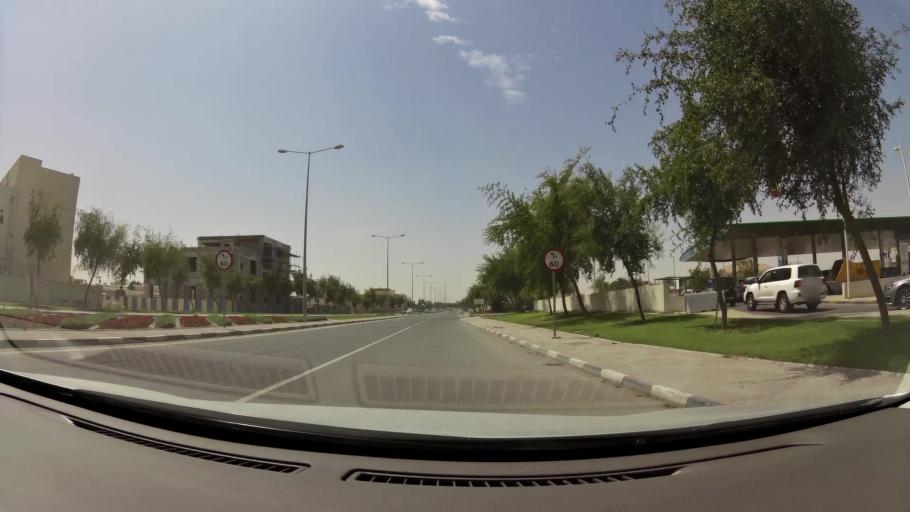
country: QA
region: Baladiyat ar Rayyan
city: Ar Rayyan
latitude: 25.2557
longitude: 51.4304
